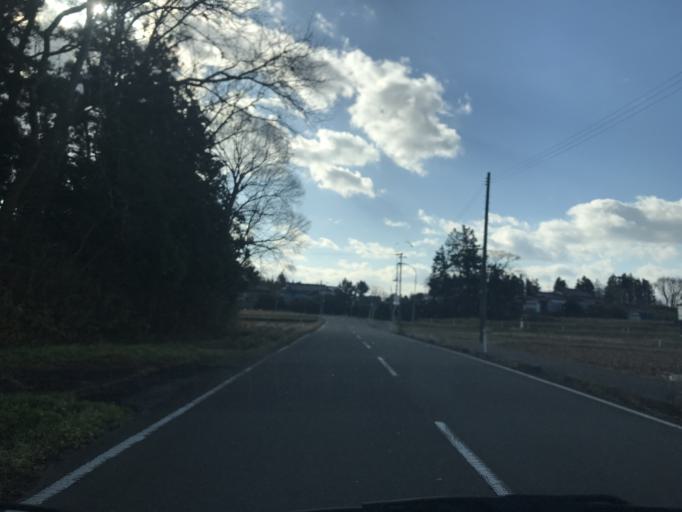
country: JP
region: Iwate
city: Ichinoseki
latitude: 38.7616
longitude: 141.0589
